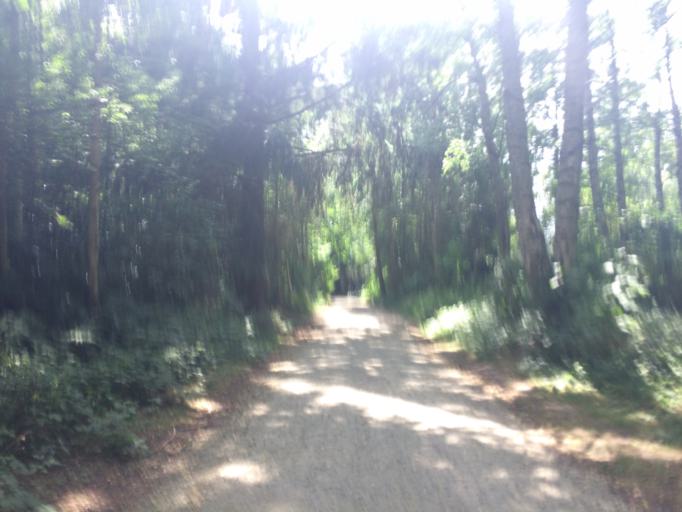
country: DK
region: Capital Region
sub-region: Bornholm Kommune
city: Ronne
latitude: 55.1202
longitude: 14.7050
